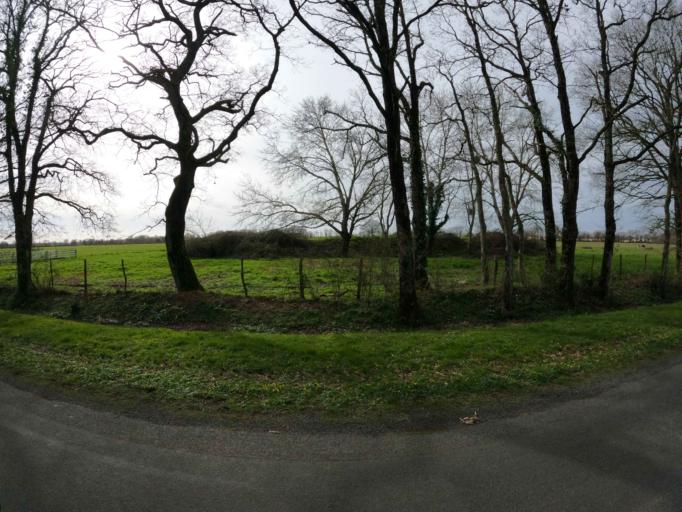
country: FR
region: Pays de la Loire
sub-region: Departement de la Vendee
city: Bouffere
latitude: 46.9605
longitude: -1.3294
